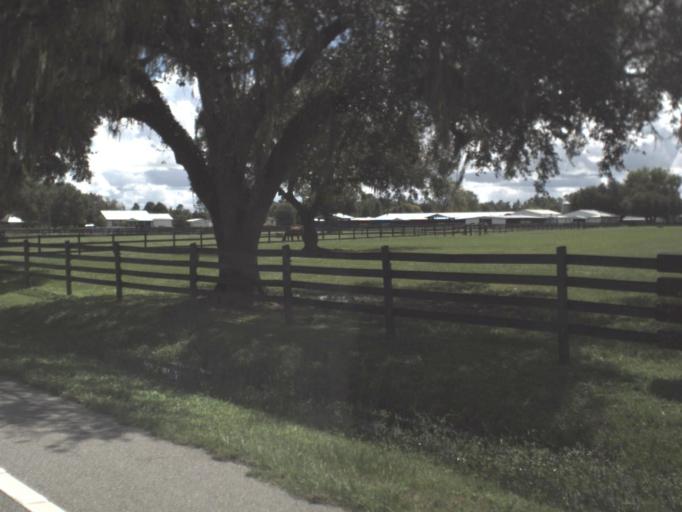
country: US
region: Florida
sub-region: Sarasota County
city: Lake Sarasota
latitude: 27.3549
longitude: -82.1765
